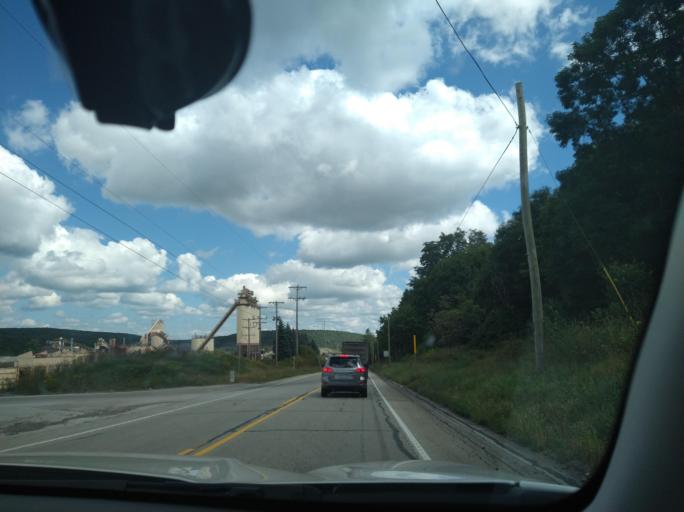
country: US
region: Pennsylvania
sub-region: Westmoreland County
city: Ligonier
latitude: 40.0671
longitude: -79.2603
